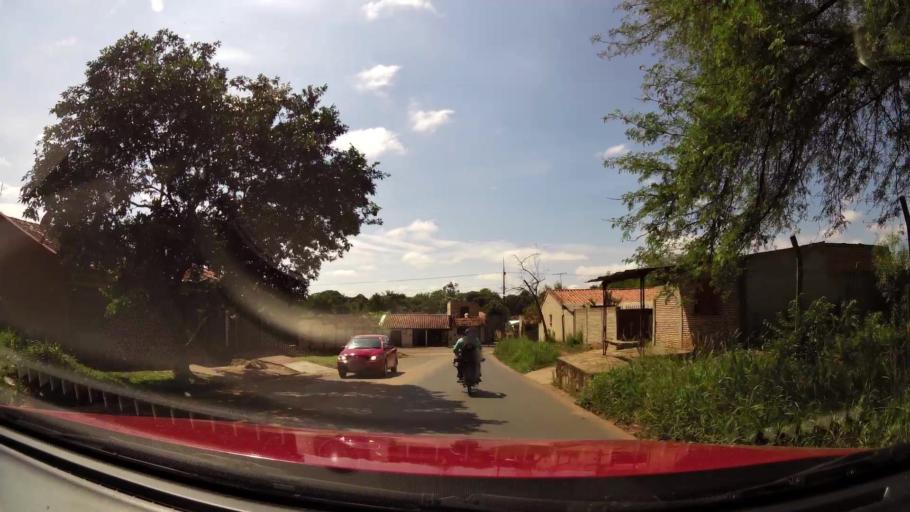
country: PY
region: Central
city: San Lorenzo
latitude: -25.2567
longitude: -57.4944
